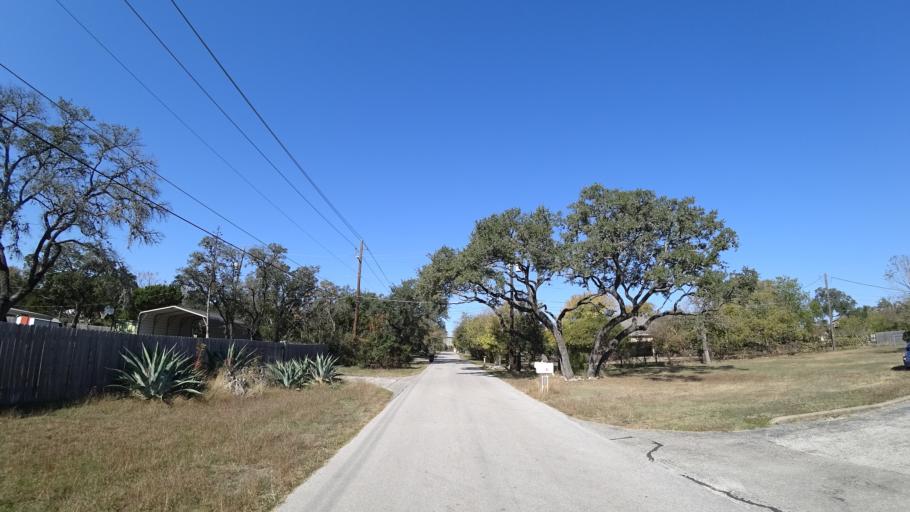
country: US
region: Texas
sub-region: Travis County
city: Barton Creek
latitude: 30.2284
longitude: -97.8584
